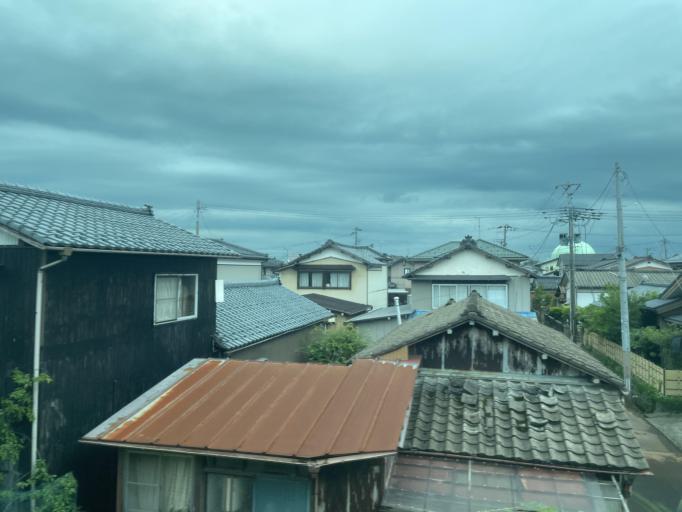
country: JP
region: Niigata
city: Yoshida-kasugacho
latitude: 37.6839
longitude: 138.8723
